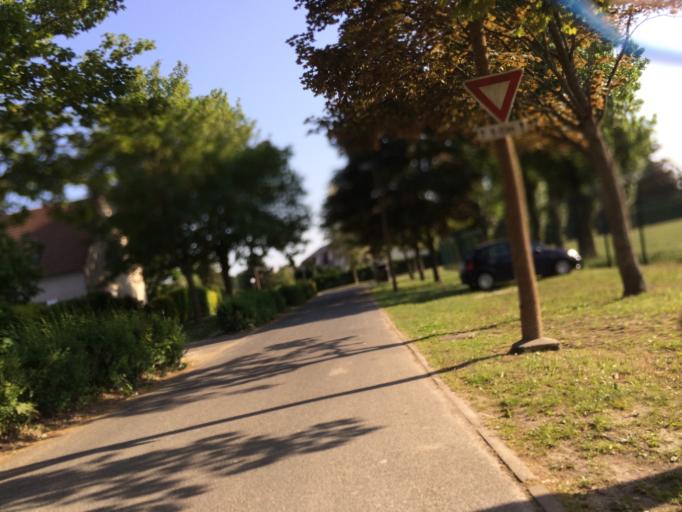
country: FR
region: Ile-de-France
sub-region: Departement de l'Essonne
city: Bondoufle
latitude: 48.6154
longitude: 2.3876
